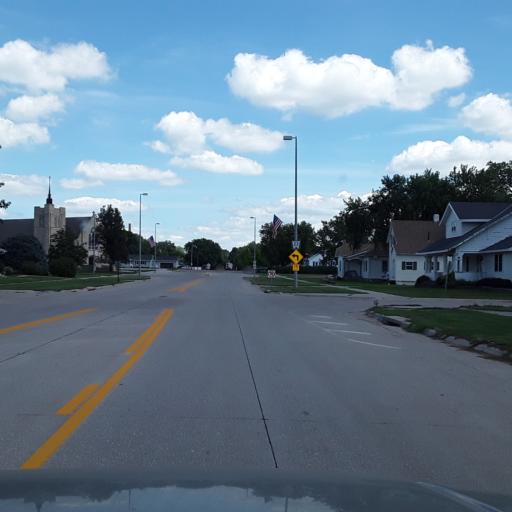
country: US
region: Nebraska
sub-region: Nance County
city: Genoa
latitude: 41.4485
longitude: -97.7273
